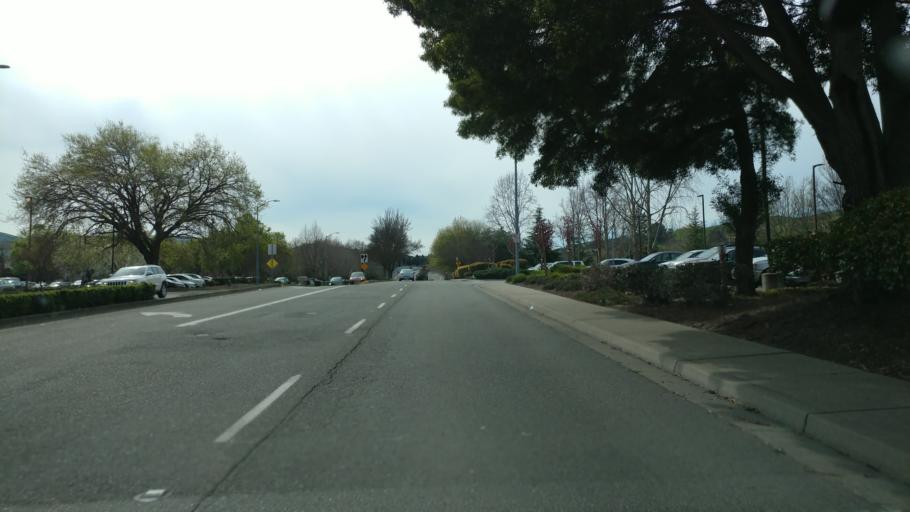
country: US
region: California
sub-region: Contra Costa County
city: San Ramon
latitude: 37.7819
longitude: -121.9715
